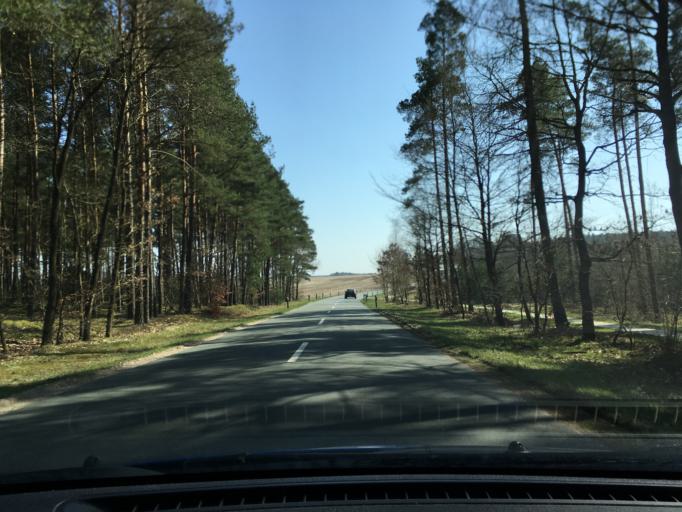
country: DE
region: Lower Saxony
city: Eimke
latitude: 52.9902
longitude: 10.3058
